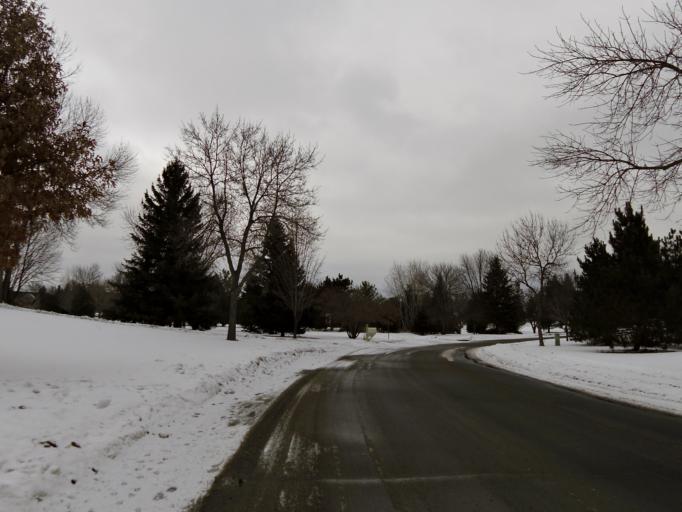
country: US
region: Minnesota
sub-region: Washington County
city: Lake Elmo
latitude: 44.9584
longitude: -92.8508
